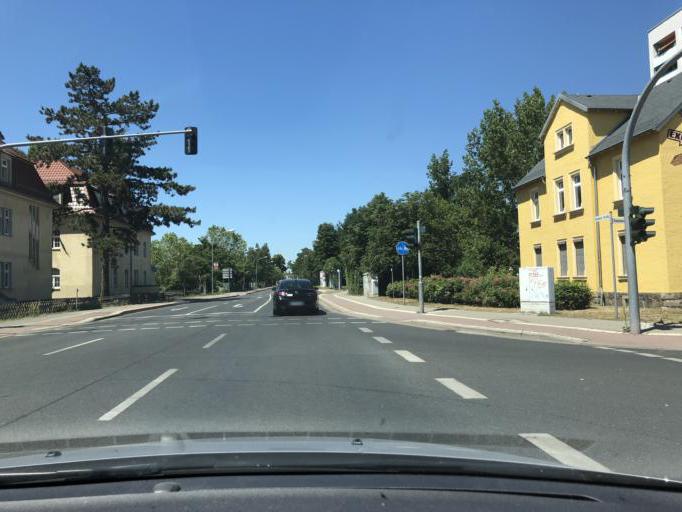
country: DE
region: Saxony
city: Coswig
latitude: 51.1231
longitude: 13.5875
